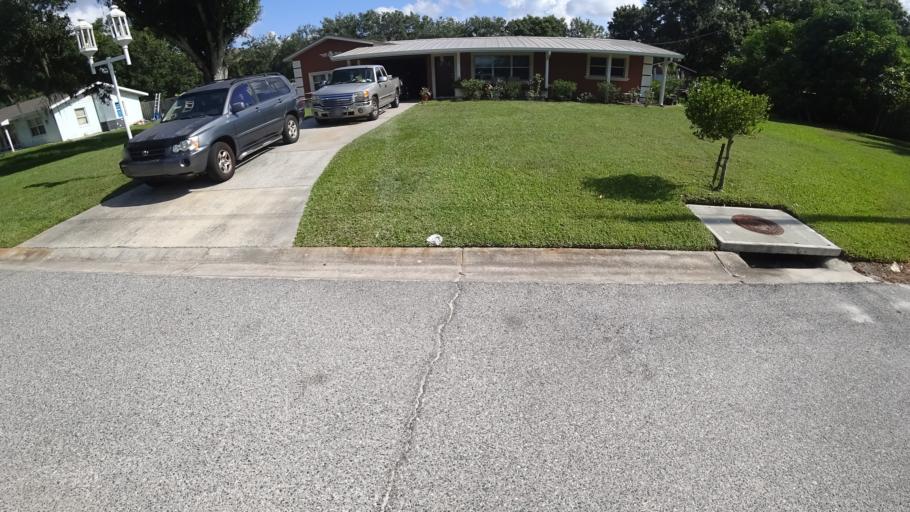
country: US
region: Florida
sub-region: Manatee County
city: Samoset
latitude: 27.4416
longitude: -82.5445
